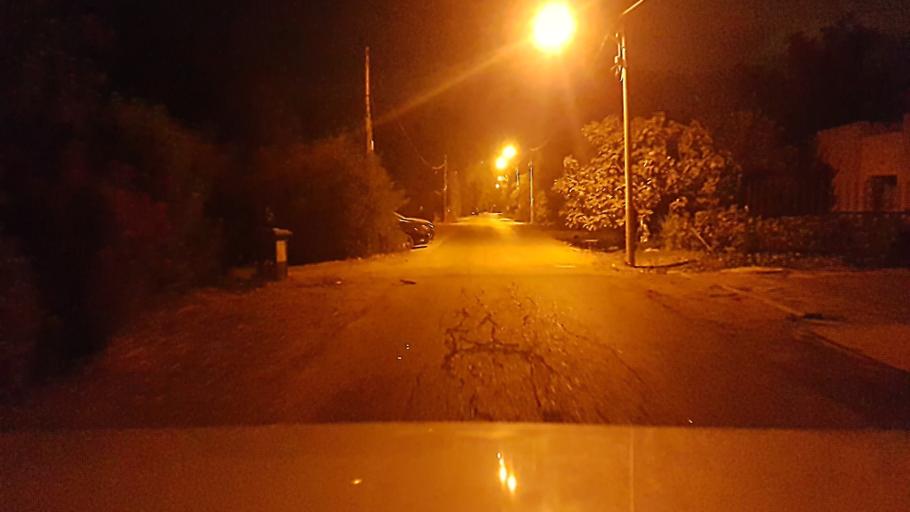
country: IL
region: Central District
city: Nehalim
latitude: 32.0792
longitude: 34.9286
